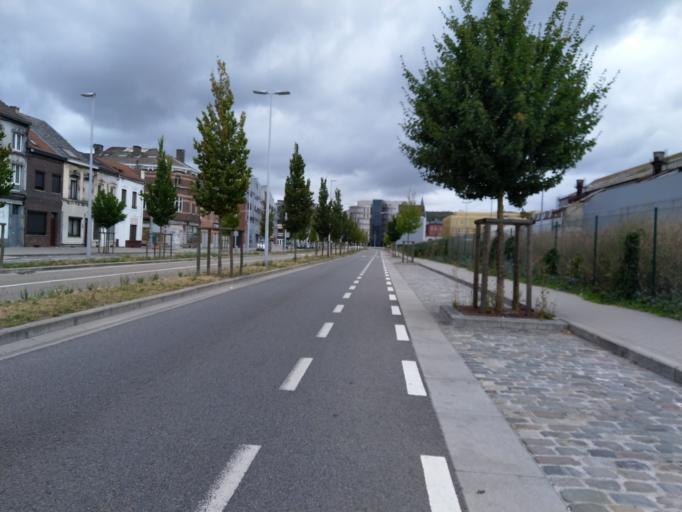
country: BE
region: Wallonia
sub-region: Province de Liege
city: Saint-Nicolas
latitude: 50.6125
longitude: 5.5125
